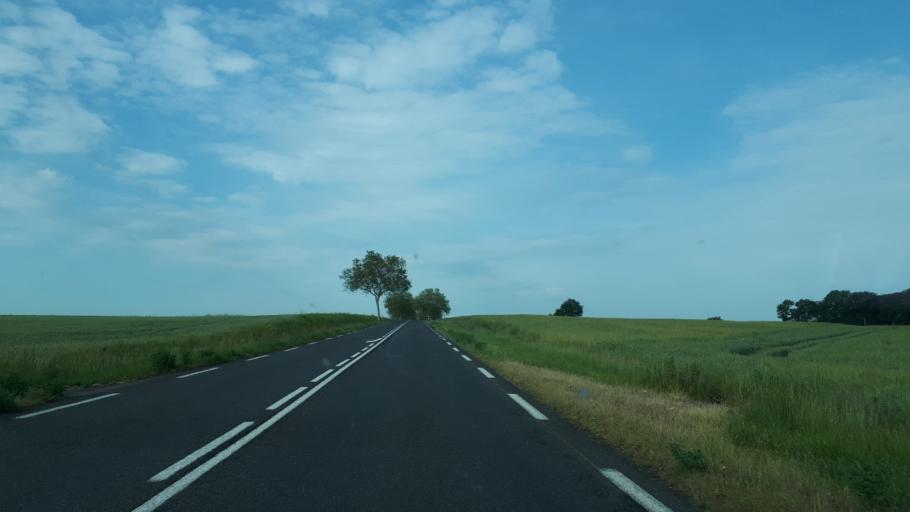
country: FR
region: Centre
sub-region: Departement d'Indre-et-Loire
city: Villedomer
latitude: 47.5410
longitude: 0.8538
